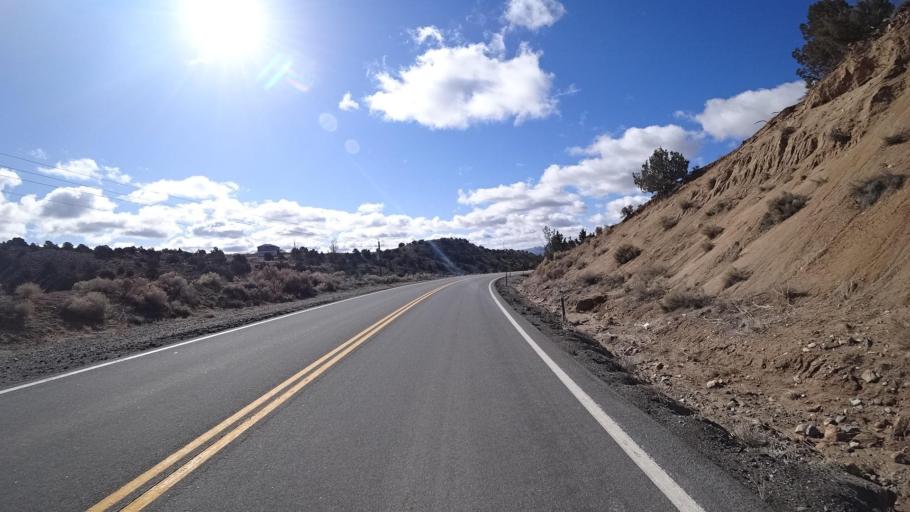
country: US
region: Nevada
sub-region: Washoe County
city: Lemmon Valley
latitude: 39.7333
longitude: -119.8812
